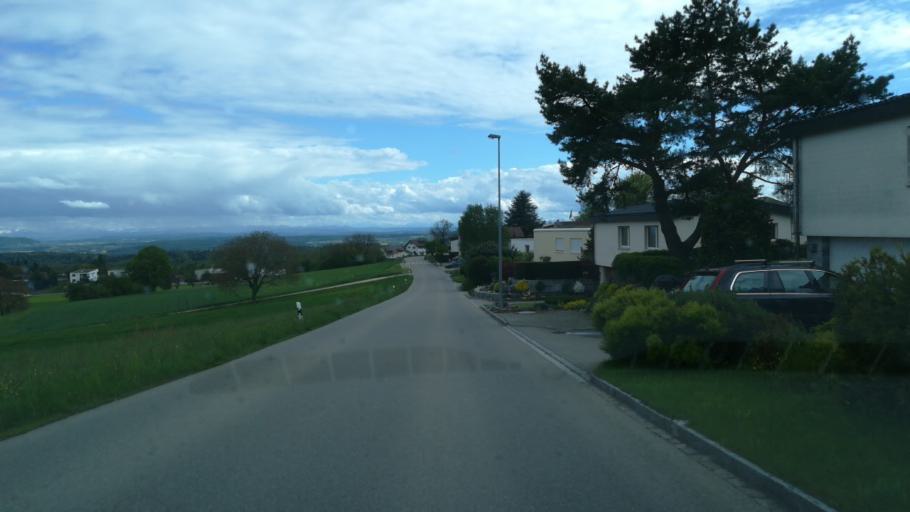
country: CH
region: Schaffhausen
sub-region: Bezirk Reiat
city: Stetten
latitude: 47.7446
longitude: 8.6626
